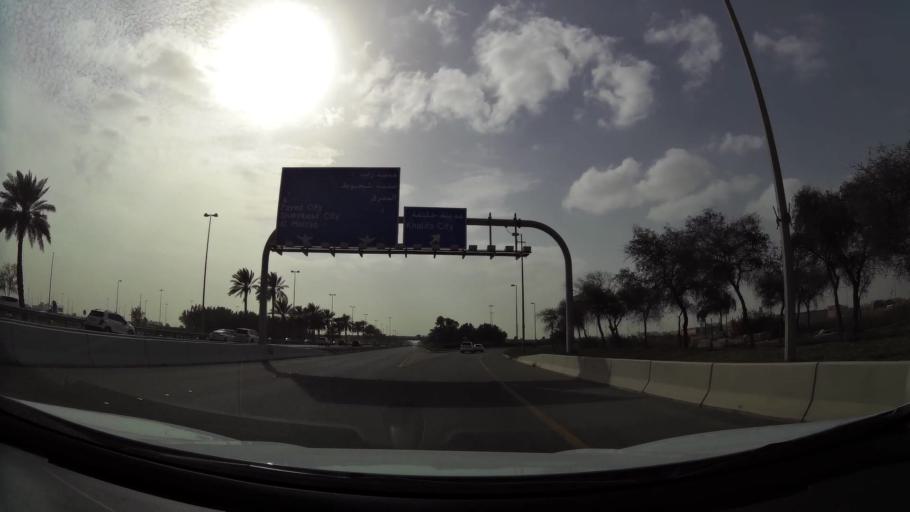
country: AE
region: Abu Dhabi
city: Abu Dhabi
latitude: 24.3988
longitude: 54.5789
